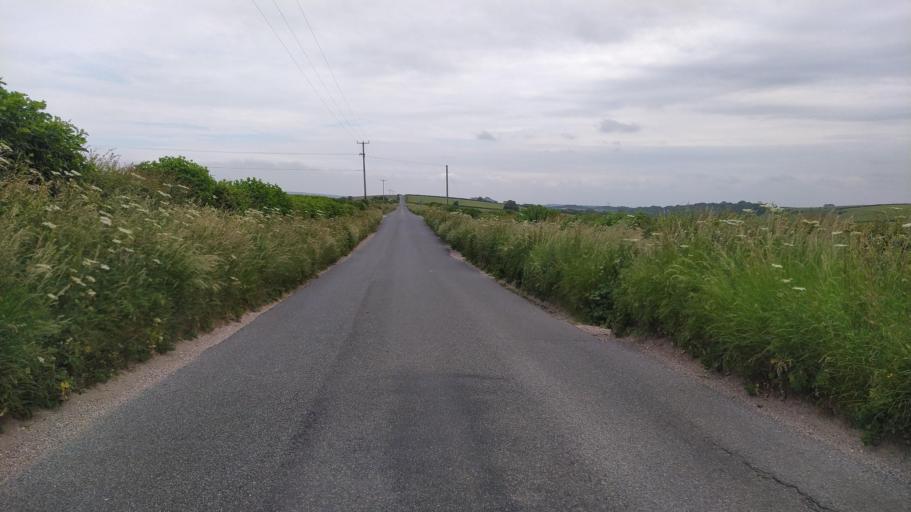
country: GB
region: England
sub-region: Dorset
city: Dorchester
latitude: 50.7656
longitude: -2.4384
